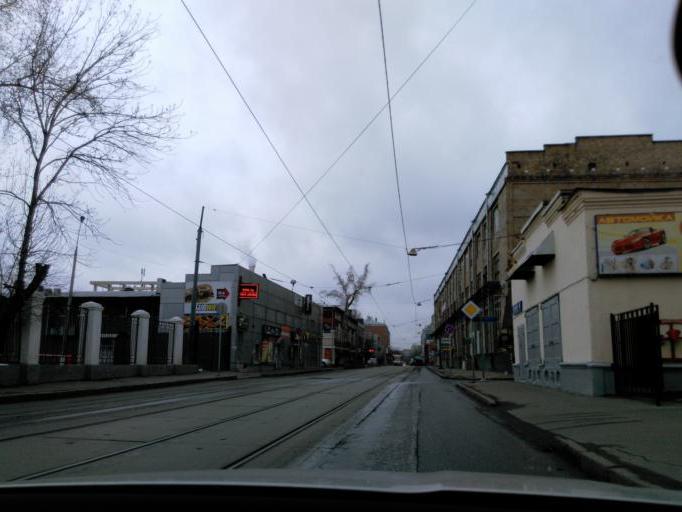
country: RU
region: Moscow
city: Zamoskvorech'ye
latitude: 55.7224
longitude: 37.6359
